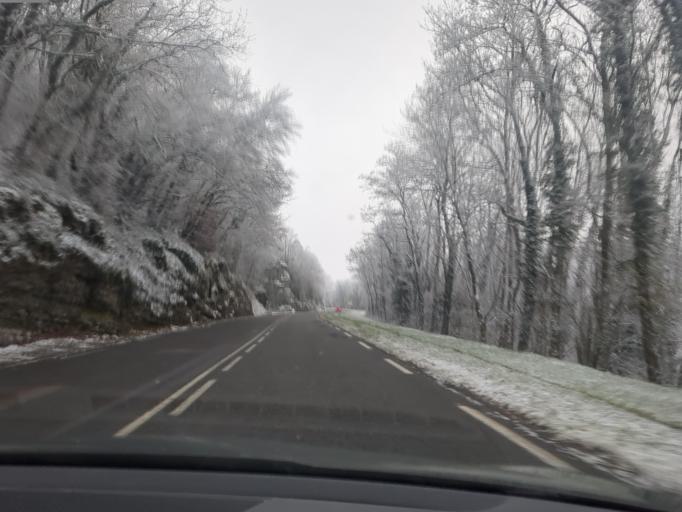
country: FR
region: Franche-Comte
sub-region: Departement du Jura
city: Perrigny
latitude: 46.6217
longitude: 5.6109
